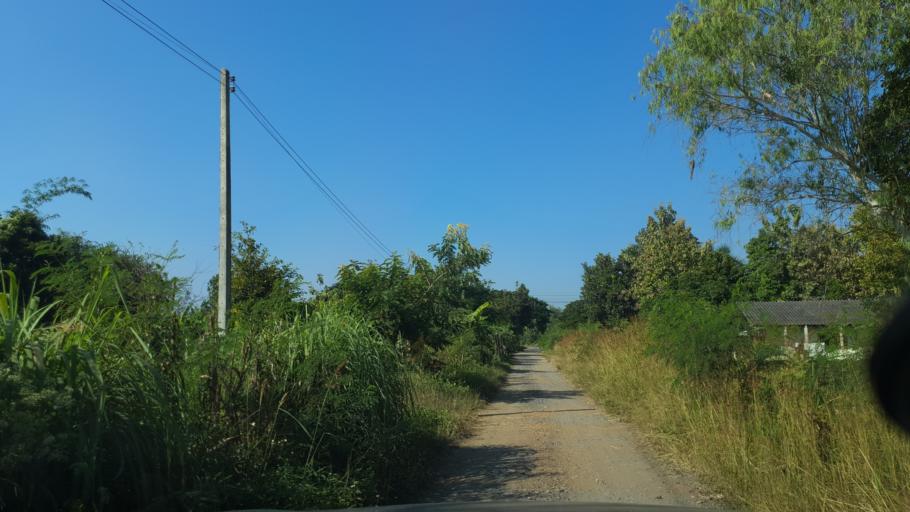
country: TH
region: Chiang Mai
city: San Kamphaeng
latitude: 18.7336
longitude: 99.1512
